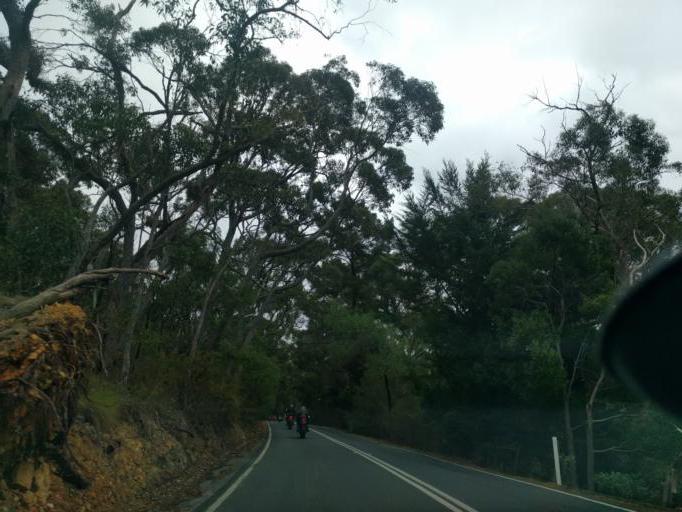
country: AU
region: South Australia
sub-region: Adelaide Hills
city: Stirling
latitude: -35.0251
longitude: 138.7580
